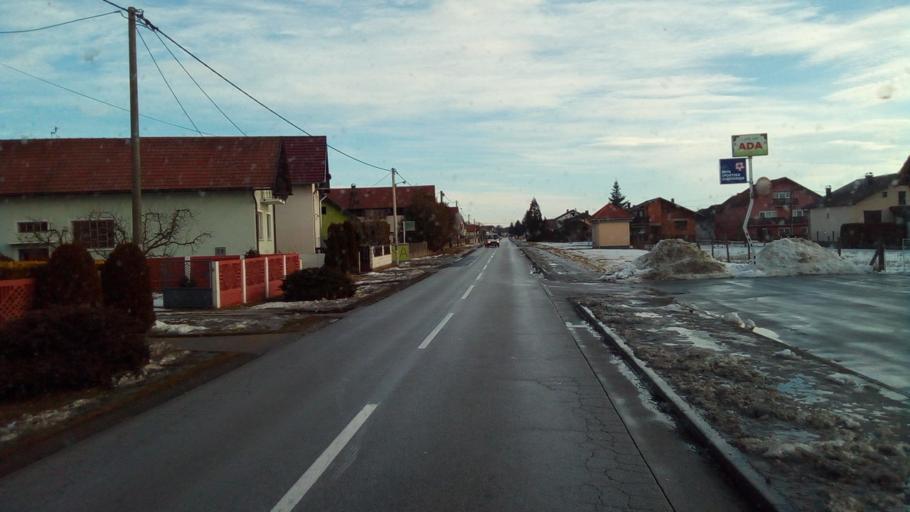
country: HR
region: Medimurska
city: Belica
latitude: 46.4010
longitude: 16.5007
